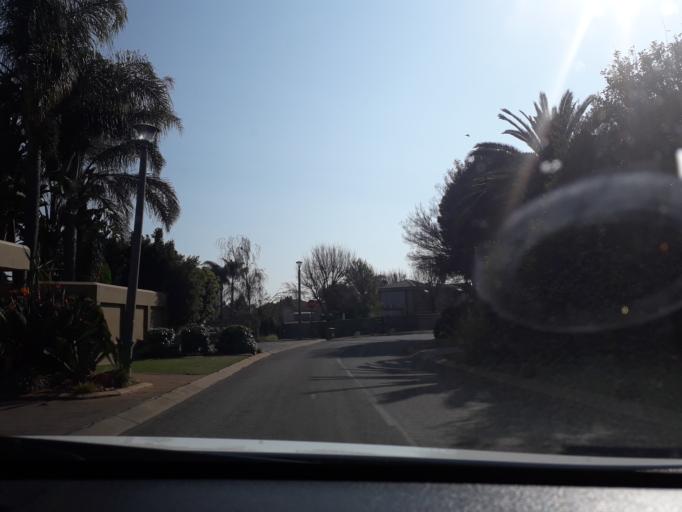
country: ZA
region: Gauteng
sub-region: Ekurhuleni Metropolitan Municipality
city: Tembisa
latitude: -26.0658
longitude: 28.2479
